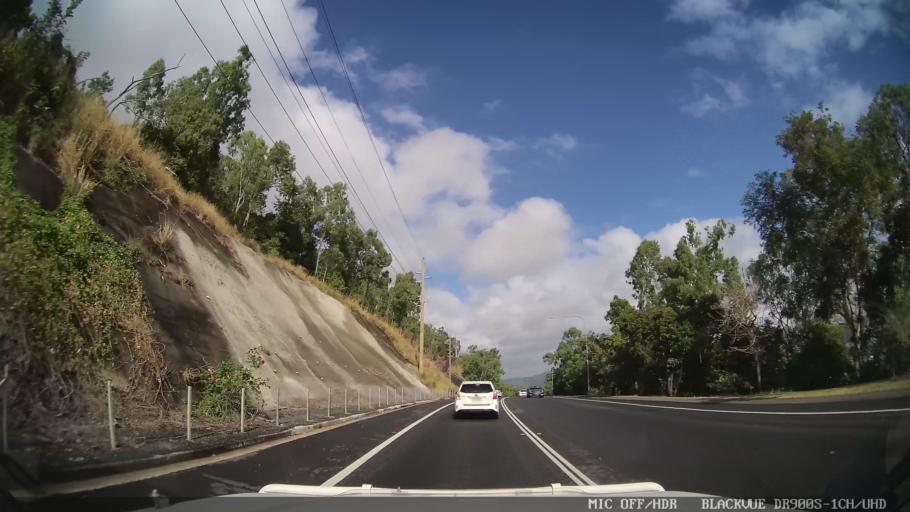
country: AU
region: Queensland
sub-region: Whitsunday
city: Proserpine
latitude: -20.2710
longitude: 148.7094
